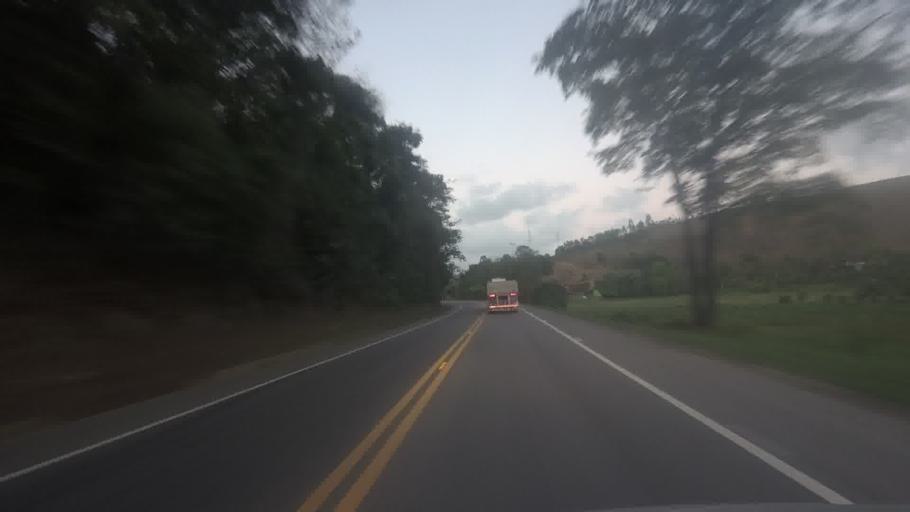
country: BR
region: Espirito Santo
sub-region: Iconha
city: Iconha
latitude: -20.8224
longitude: -40.8499
